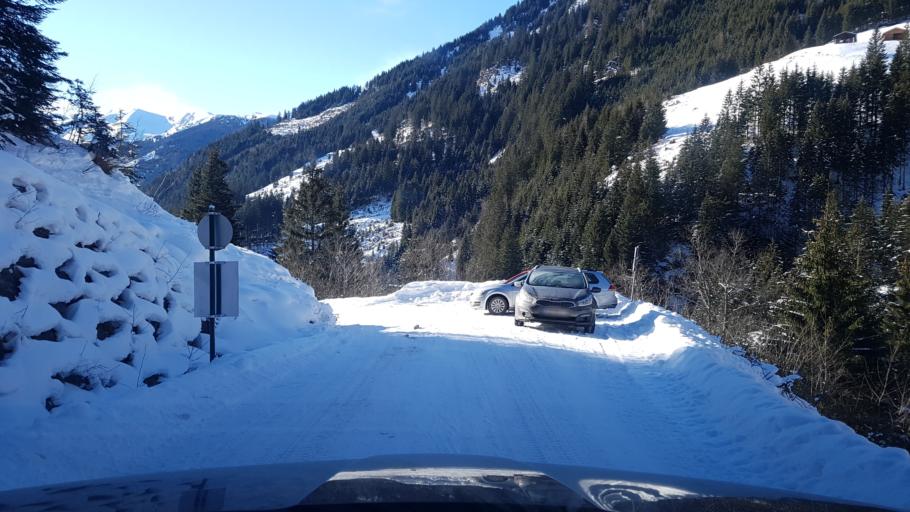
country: AT
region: Salzburg
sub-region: Politischer Bezirk Sankt Johann im Pongau
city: Huttschlag
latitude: 47.1815
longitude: 13.2702
